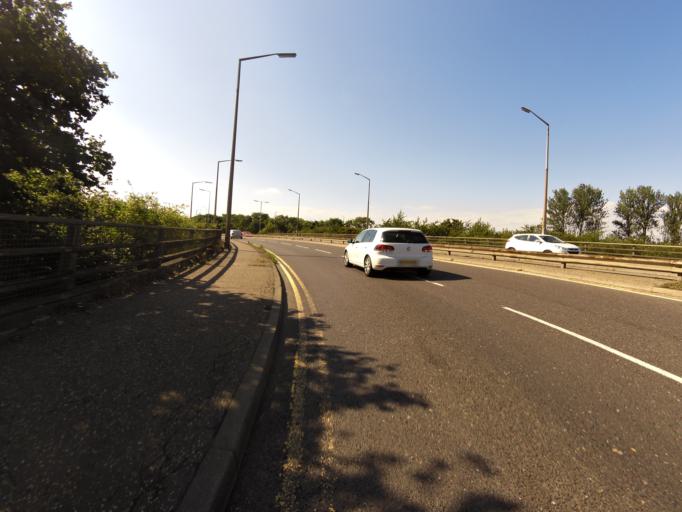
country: GB
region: England
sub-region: Essex
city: Marks Tey
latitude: 51.8803
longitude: 0.7858
